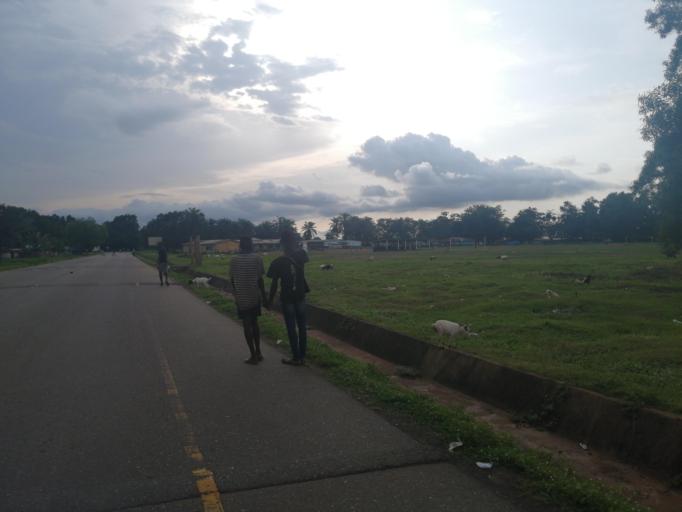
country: SL
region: Northern Province
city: Port Loko
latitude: 8.7750
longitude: -12.7909
